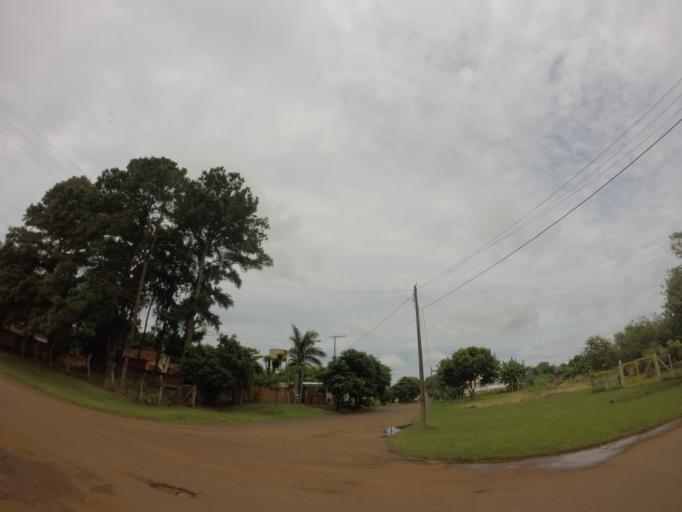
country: PY
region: Alto Parana
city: Ciudad del Este
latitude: -25.4038
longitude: -54.6391
